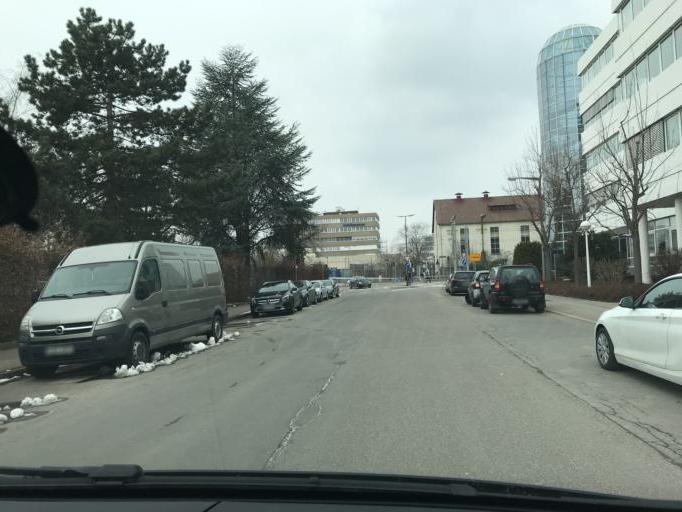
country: DE
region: Baden-Wuerttemberg
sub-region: Regierungsbezirk Stuttgart
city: Leinfelden-Echterdingen
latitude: 48.7228
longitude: 9.1225
